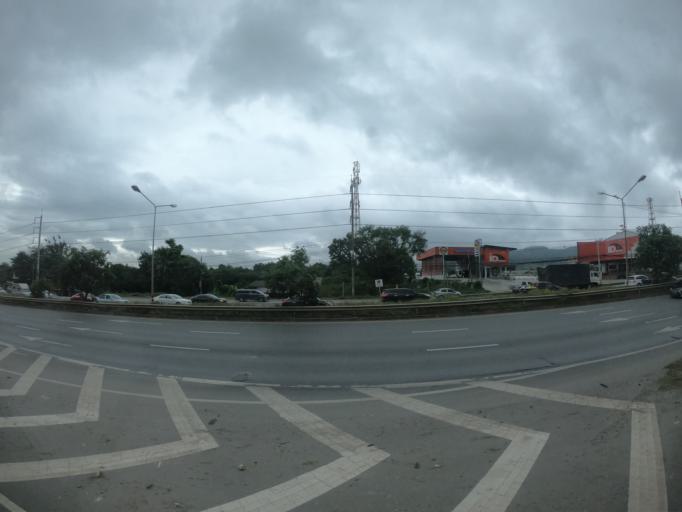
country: TH
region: Sara Buri
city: Kaeng Khoi
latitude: 14.6079
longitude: 101.0674
